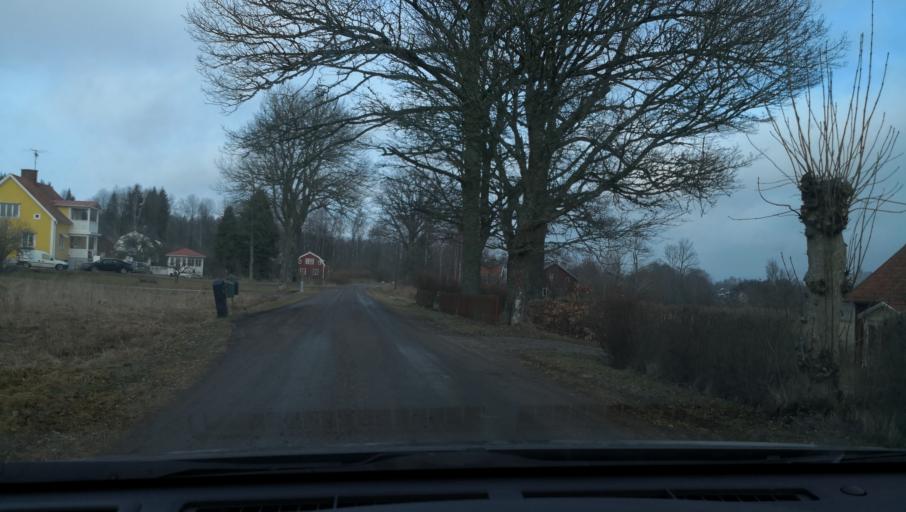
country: SE
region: Vaestra Goetaland
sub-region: Gullspangs Kommun
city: Gullspang
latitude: 58.9615
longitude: 14.0927
